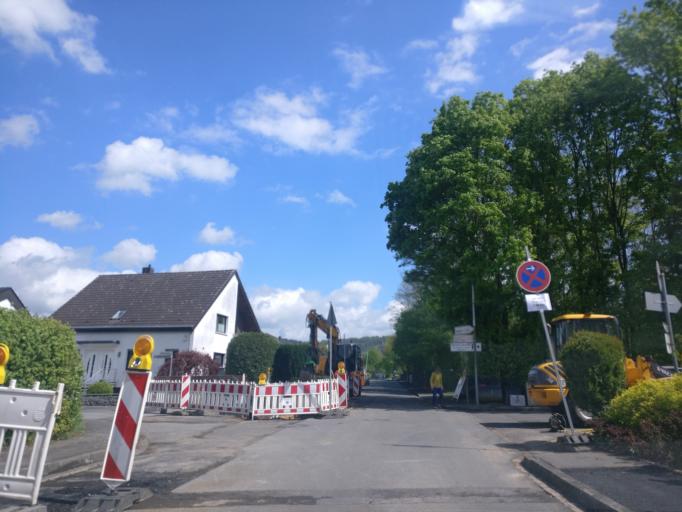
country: DE
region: Lower Saxony
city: Hannoversch Munden
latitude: 51.4339
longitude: 9.6444
